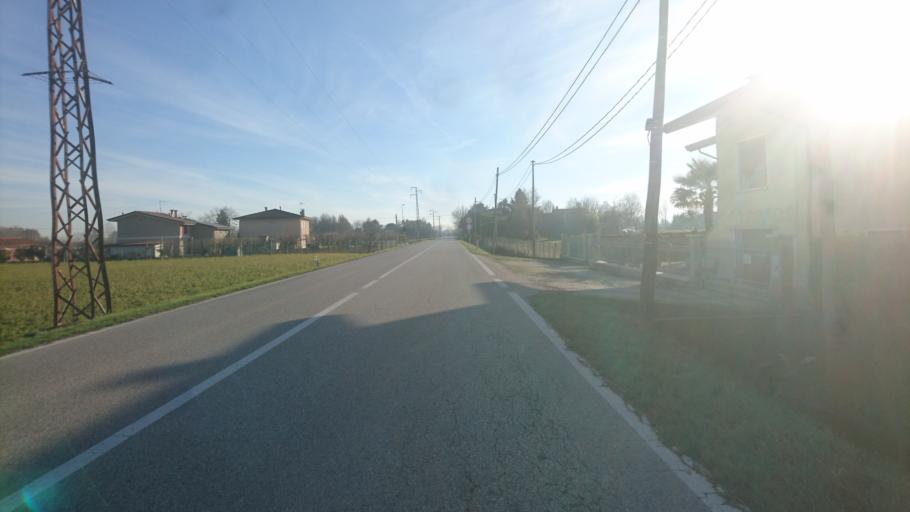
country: IT
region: Veneto
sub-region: Provincia di Padova
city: Tremignon
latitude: 45.5145
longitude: 11.7860
